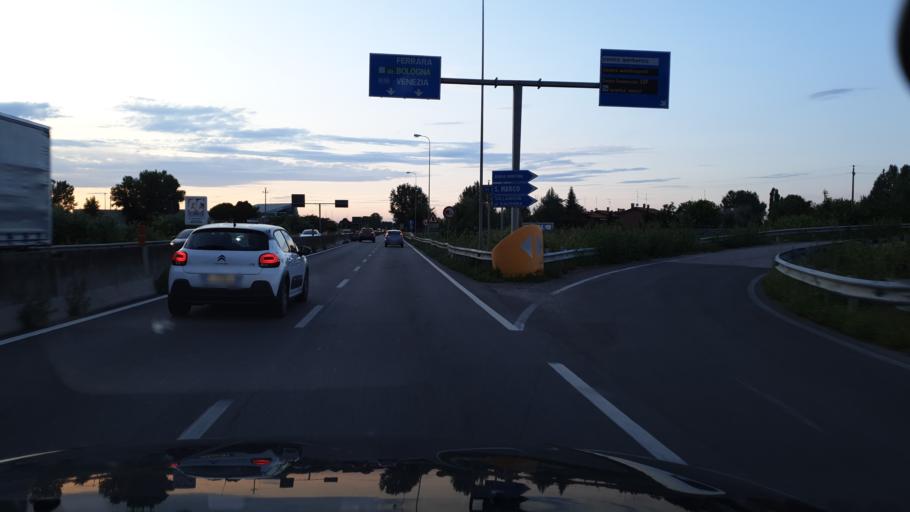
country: IT
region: Emilia-Romagna
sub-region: Provincia di Ravenna
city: Ravenna
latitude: 44.4111
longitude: 12.1724
